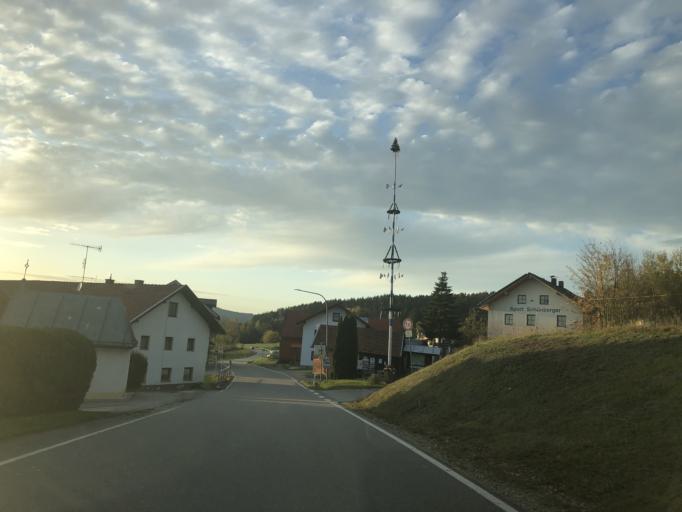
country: DE
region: Bavaria
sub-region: Lower Bavaria
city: Langdorf
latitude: 49.0150
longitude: 13.1896
